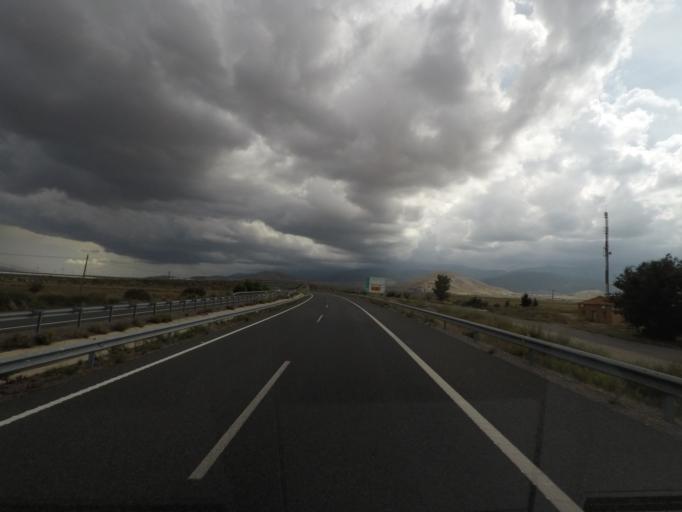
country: ES
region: Andalusia
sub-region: Provincia de Granada
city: Aldeire
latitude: 37.2130
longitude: -3.0703
